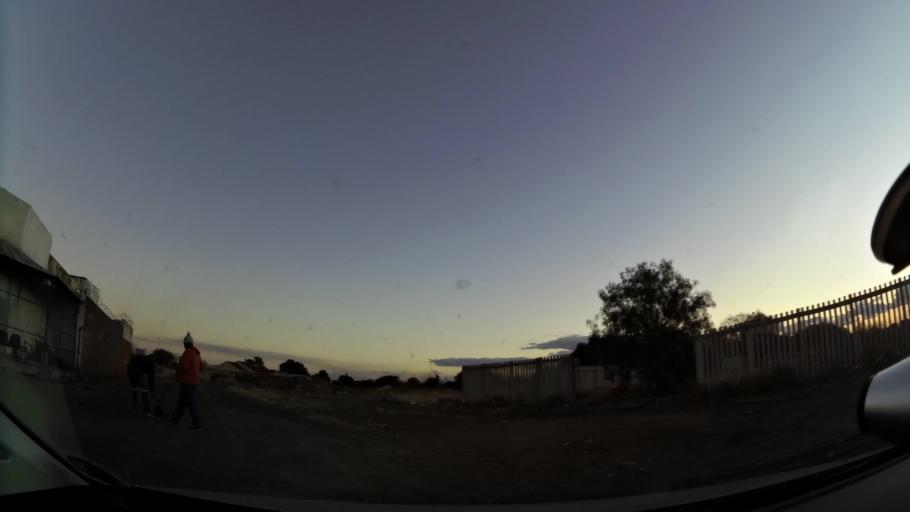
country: ZA
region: Northern Cape
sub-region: Frances Baard District Municipality
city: Kimberley
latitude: -28.7178
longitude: 24.7663
